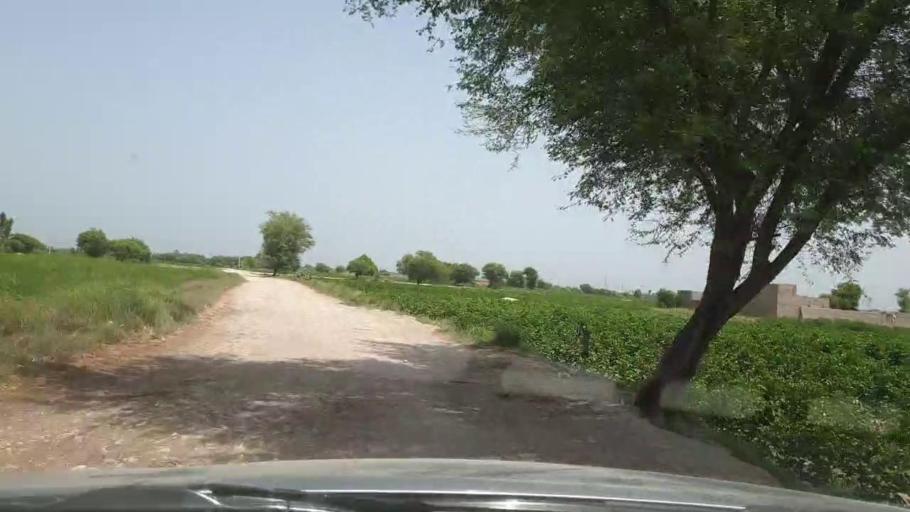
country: PK
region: Sindh
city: Pano Aqil
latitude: 27.8306
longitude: 69.1979
